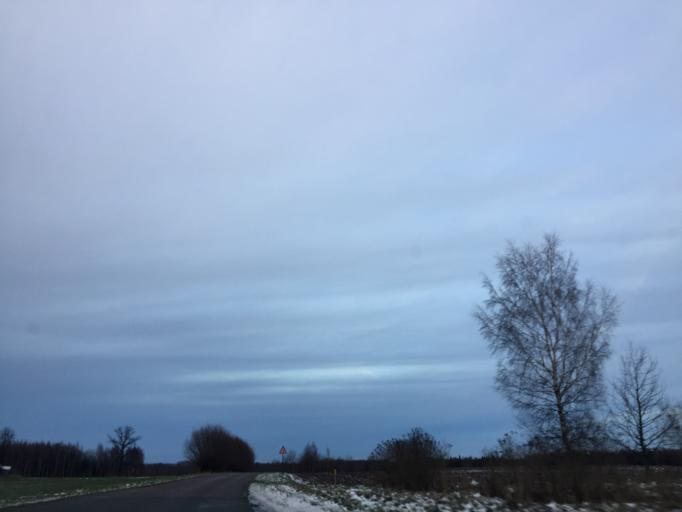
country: LV
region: Aloja
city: Aloja
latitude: 57.6220
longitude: 24.9290
